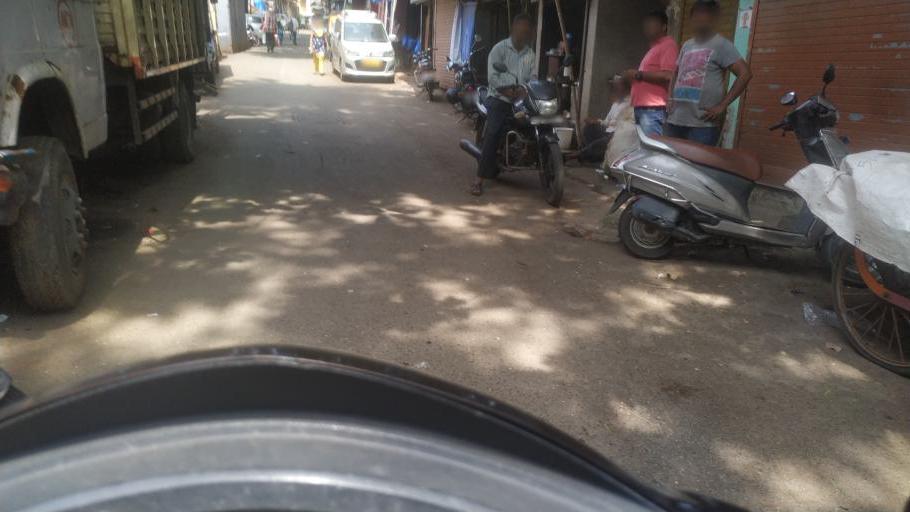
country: IN
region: Maharashtra
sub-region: Mumbai Suburban
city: Mumbai
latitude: 19.0011
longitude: 72.8466
